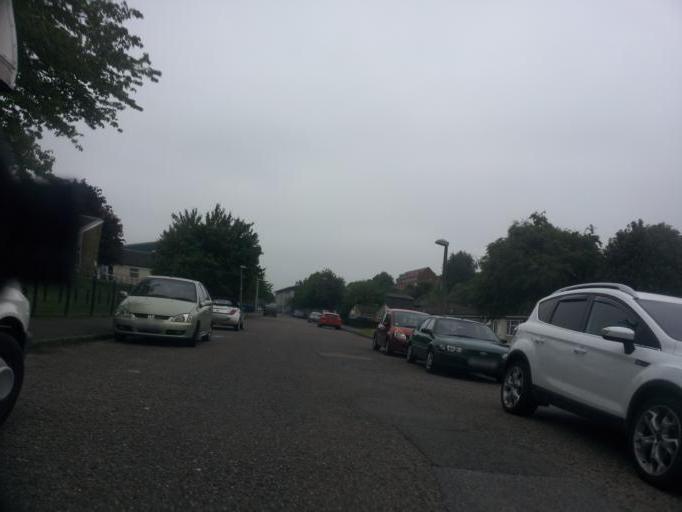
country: GB
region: England
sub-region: Kent
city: Chatham
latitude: 51.3661
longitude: 0.5470
